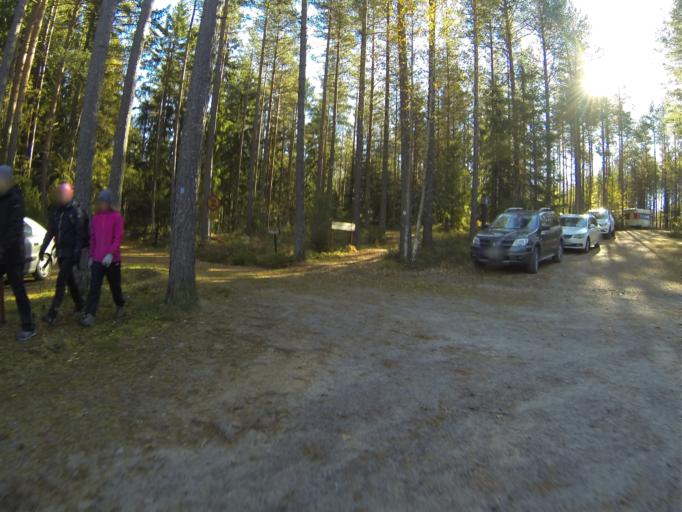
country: FI
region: Varsinais-Suomi
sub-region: Salo
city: Saerkisalo
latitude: 60.2091
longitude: 22.9386
